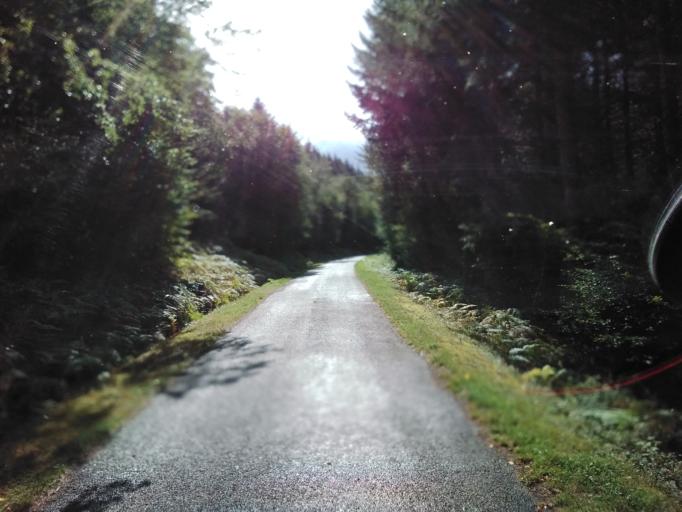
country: FR
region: Bourgogne
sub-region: Departement de la Nievre
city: Lormes
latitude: 47.3277
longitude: 3.9001
